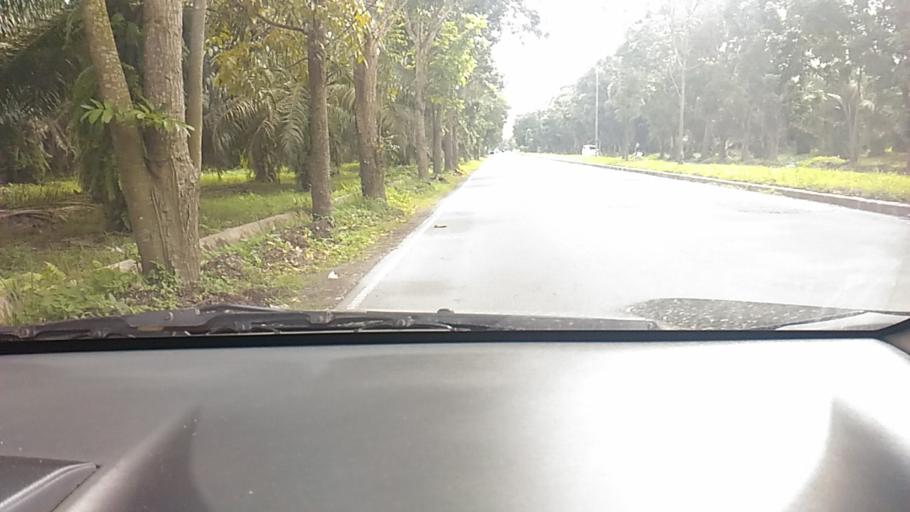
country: ID
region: North Sumatra
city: Binjai
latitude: 3.6509
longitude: 98.5260
